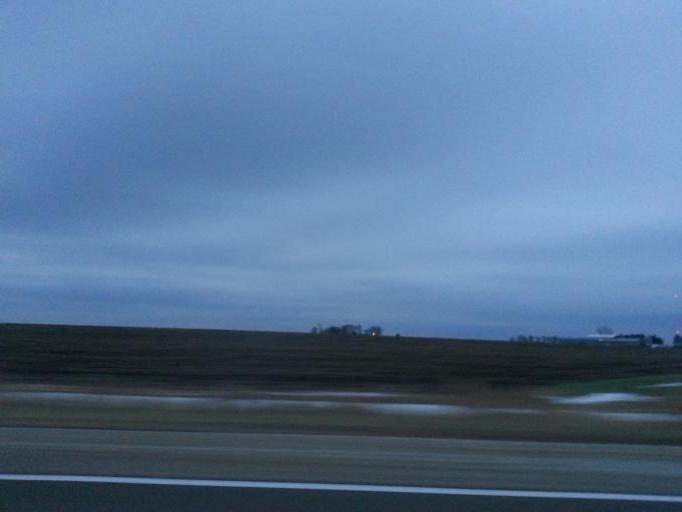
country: US
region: Iowa
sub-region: Black Hawk County
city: La Porte City
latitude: 42.3928
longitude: -92.1385
